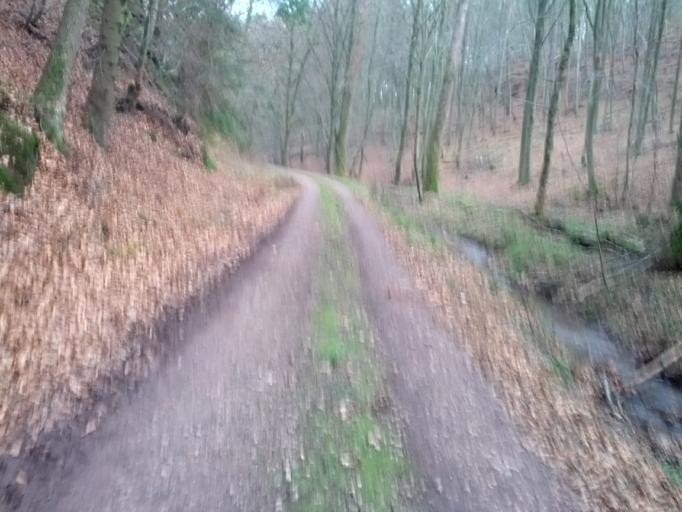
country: DE
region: Thuringia
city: Eisenach
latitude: 50.9385
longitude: 10.3352
